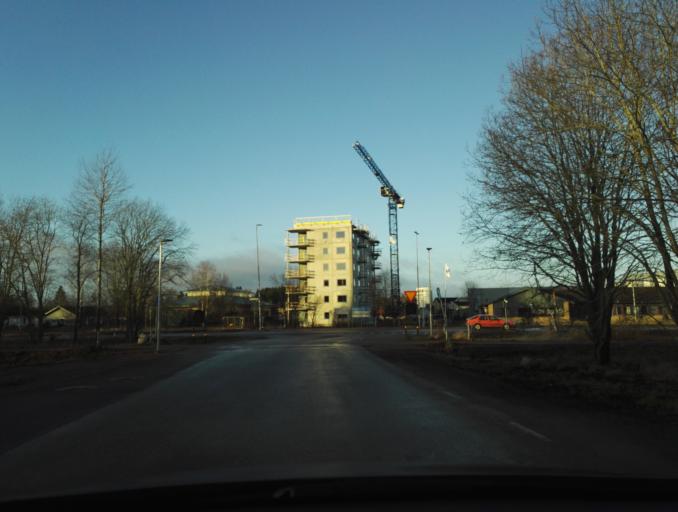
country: SE
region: Kronoberg
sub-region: Vaxjo Kommun
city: Vaexjoe
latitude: 56.9078
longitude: 14.7992
